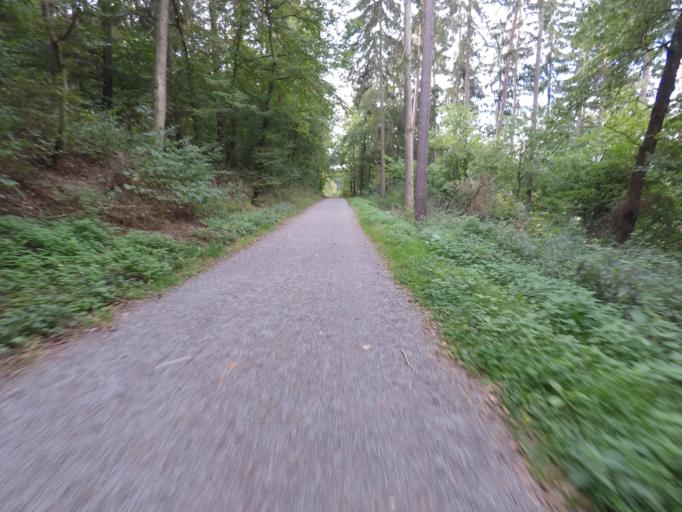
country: DE
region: Baden-Wuerttemberg
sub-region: Regierungsbezirk Stuttgart
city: Boeblingen
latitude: 48.6721
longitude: 8.9903
